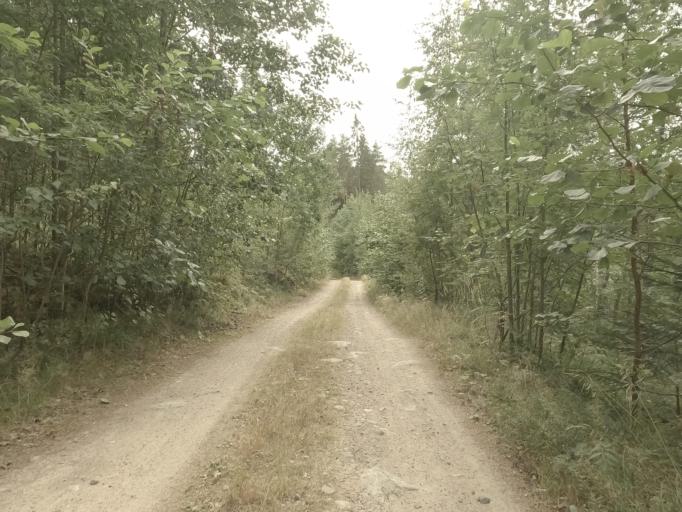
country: RU
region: Leningrad
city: Kamennogorsk
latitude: 61.0089
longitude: 29.1867
